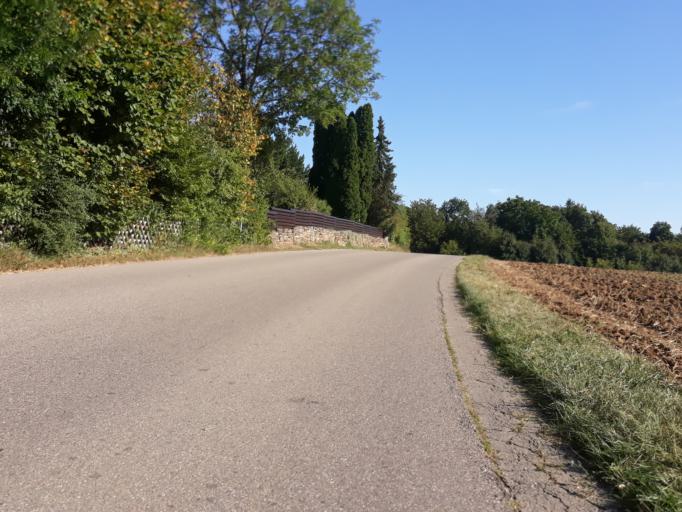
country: DE
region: Baden-Wuerttemberg
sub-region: Karlsruhe Region
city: Gechingen
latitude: 48.6909
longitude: 8.8378
